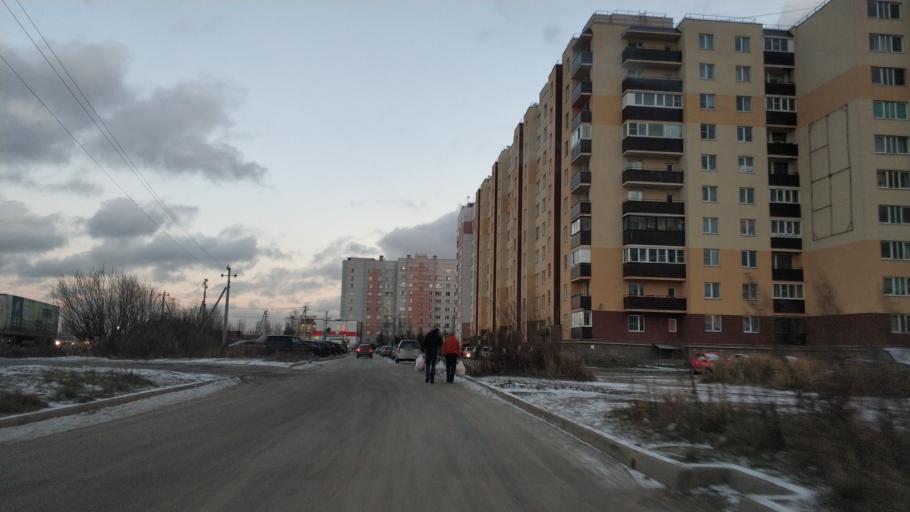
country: RU
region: St.-Petersburg
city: Pontonnyy
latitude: 59.8009
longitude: 30.6347
